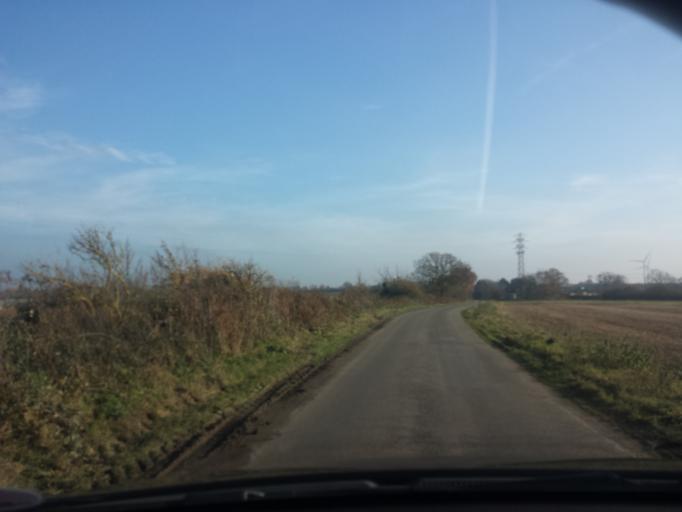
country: GB
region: England
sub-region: Essex
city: Saint Osyth
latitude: 51.8262
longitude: 1.0899
